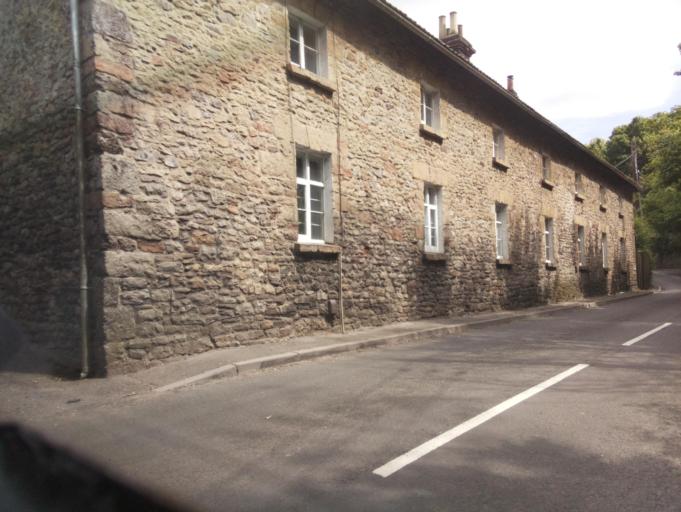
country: GB
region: England
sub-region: North Somerset
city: Easton-in-Gordano
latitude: 51.4944
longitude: -2.6590
